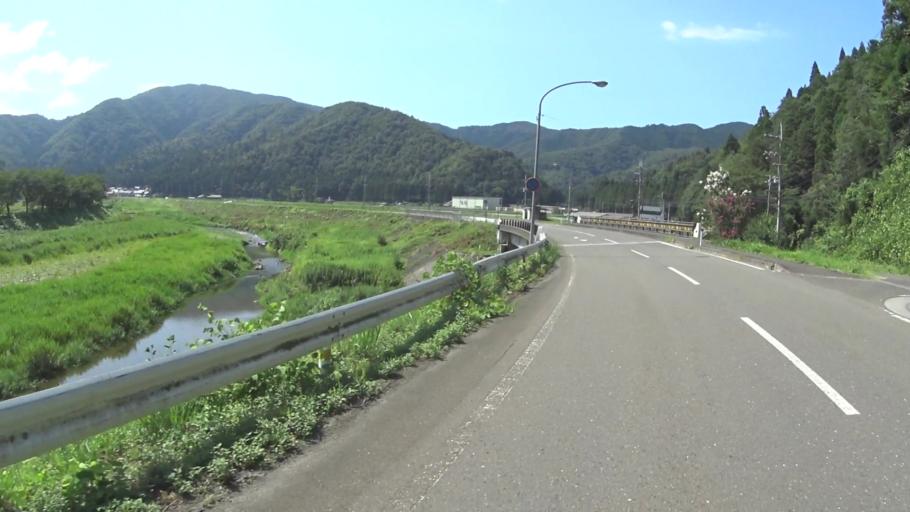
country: JP
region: Fukui
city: Obama
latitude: 35.4087
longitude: 135.6413
